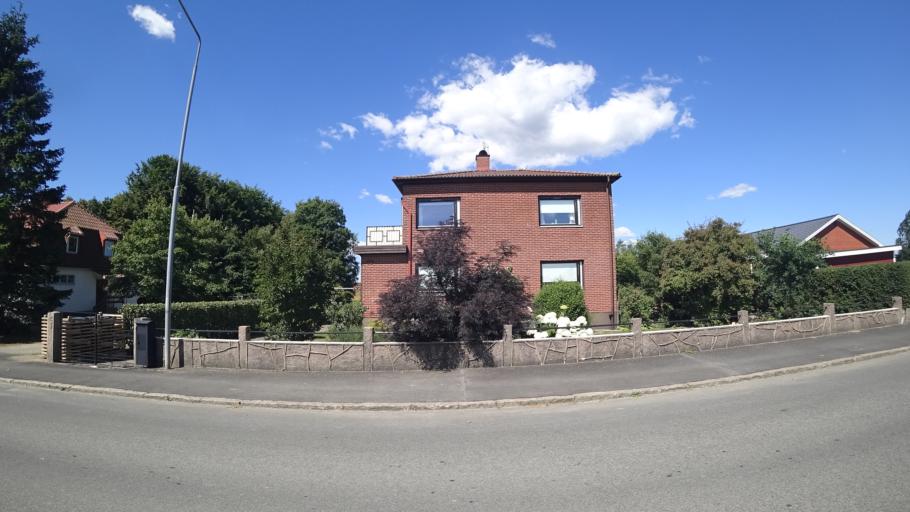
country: SE
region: Skane
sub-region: Kristianstads Kommun
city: Onnestad
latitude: 56.0636
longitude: 14.0262
